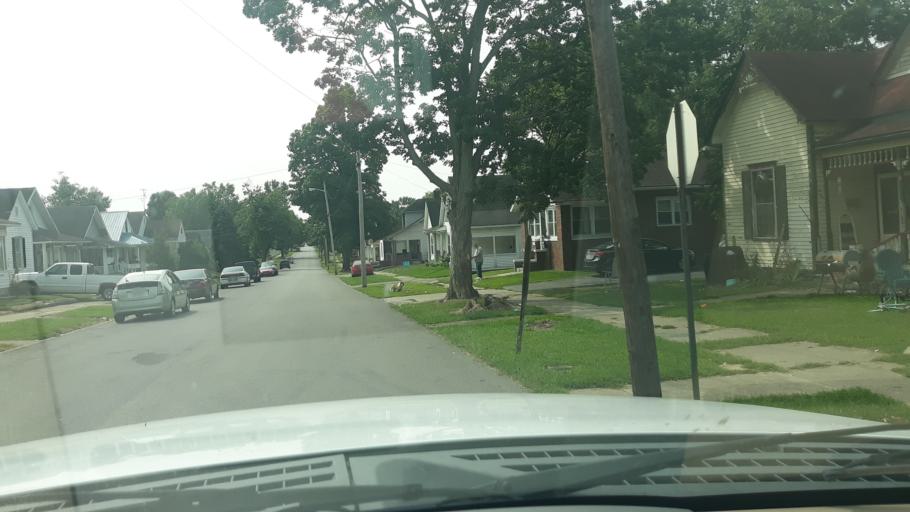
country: US
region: Indiana
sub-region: Gibson County
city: Princeton
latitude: 38.3543
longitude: -87.5638
